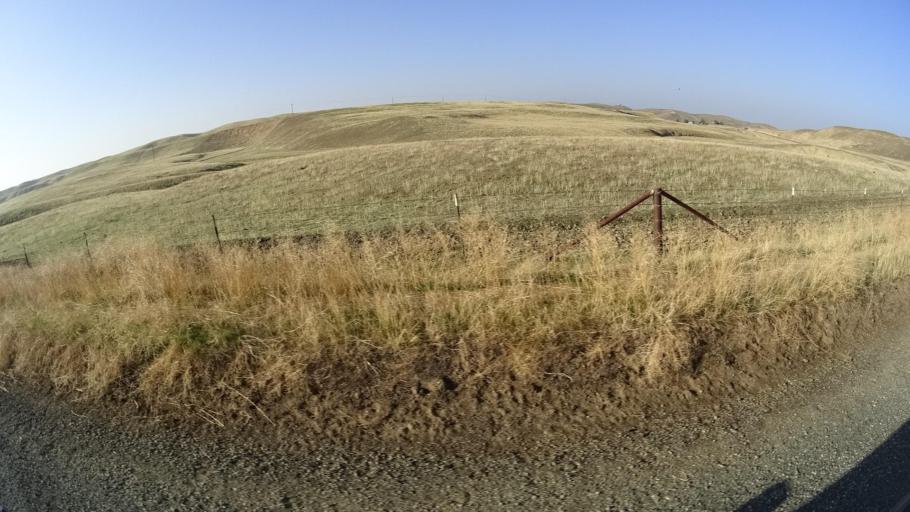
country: US
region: California
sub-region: Tulare County
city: Richgrove
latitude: 35.7451
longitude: -118.9636
